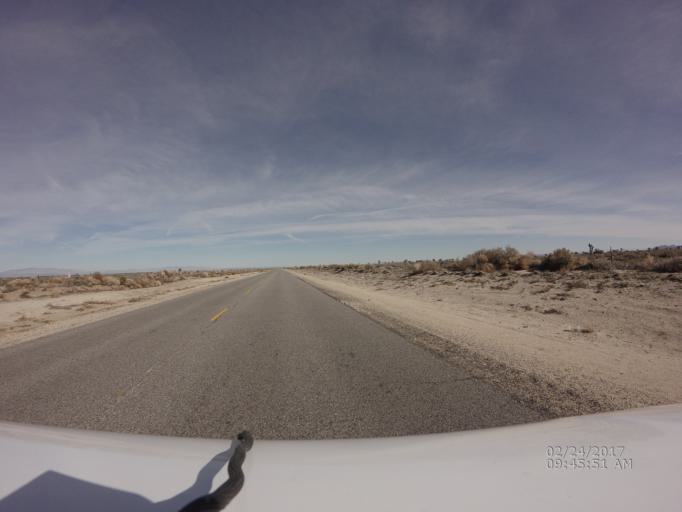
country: US
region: California
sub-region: Los Angeles County
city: Littlerock
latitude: 34.6092
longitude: -118.0052
